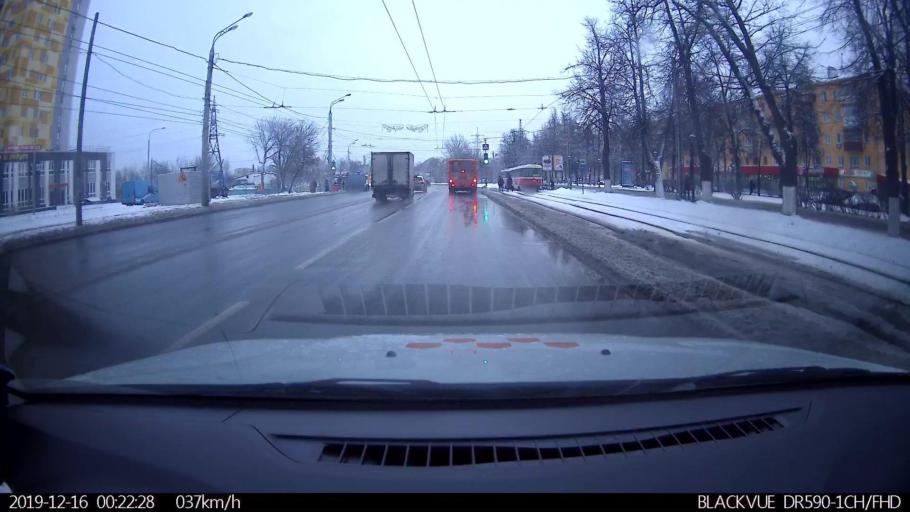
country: RU
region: Nizjnij Novgorod
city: Neklyudovo
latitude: 56.3458
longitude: 43.8720
